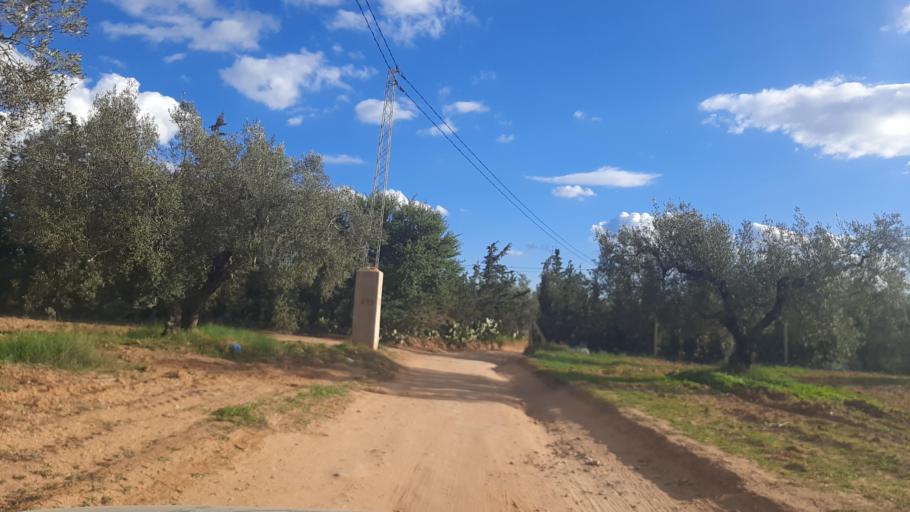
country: TN
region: Nabul
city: Al Hammamat
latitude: 36.4301
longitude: 10.5060
